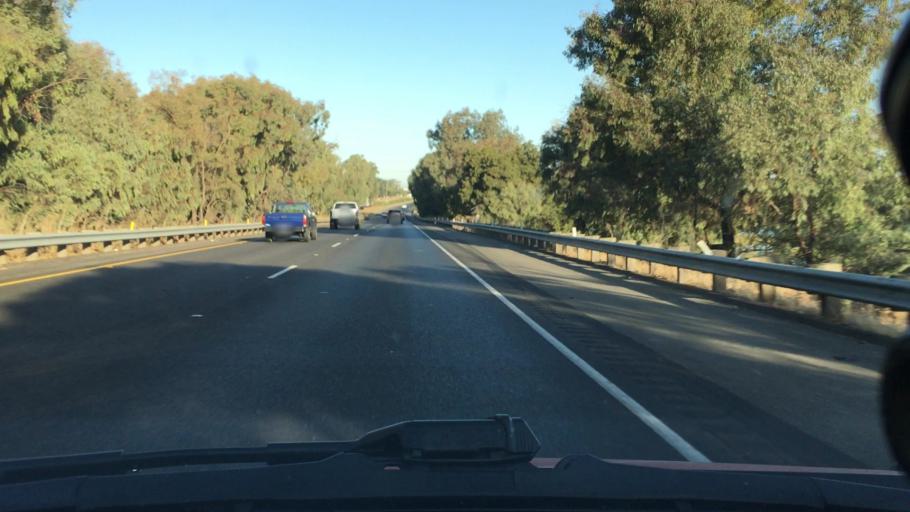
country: US
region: California
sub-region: Sacramento County
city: Elk Grove
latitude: 38.3640
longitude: -121.3489
